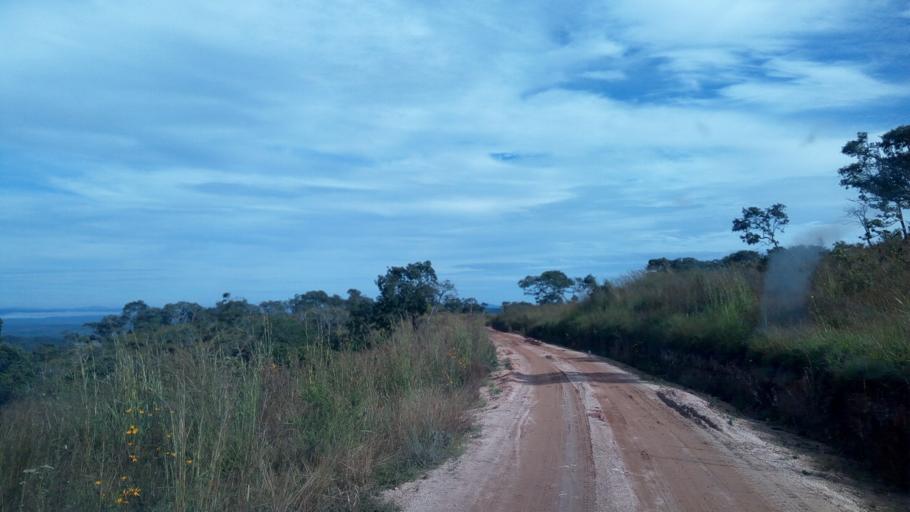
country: CD
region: Katanga
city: Kalemie
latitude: -6.2405
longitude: 28.9075
